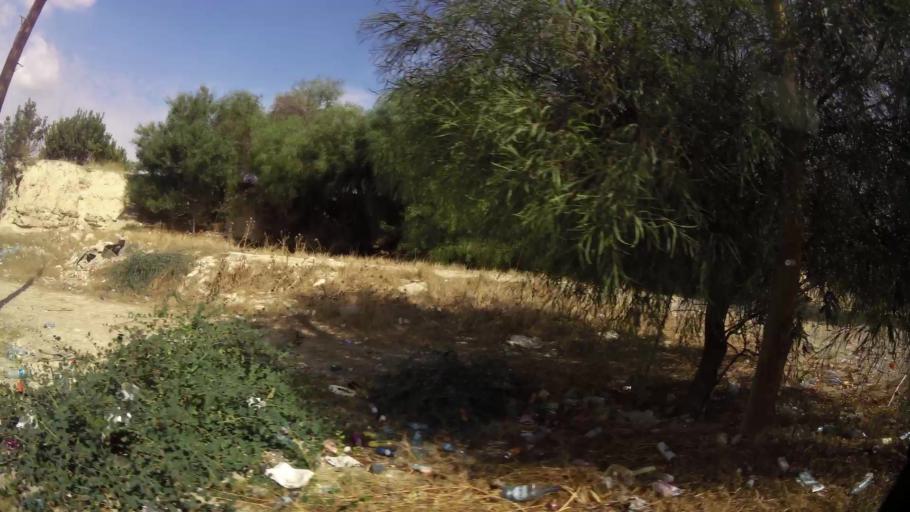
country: CY
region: Larnaka
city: Aradippou
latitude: 34.9527
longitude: 33.5830
